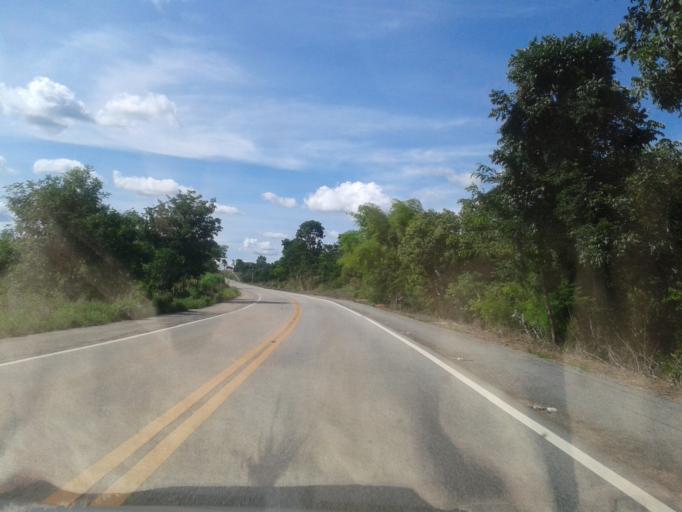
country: BR
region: Goias
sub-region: Mozarlandia
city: Mozarlandia
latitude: -15.1729
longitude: -50.5632
